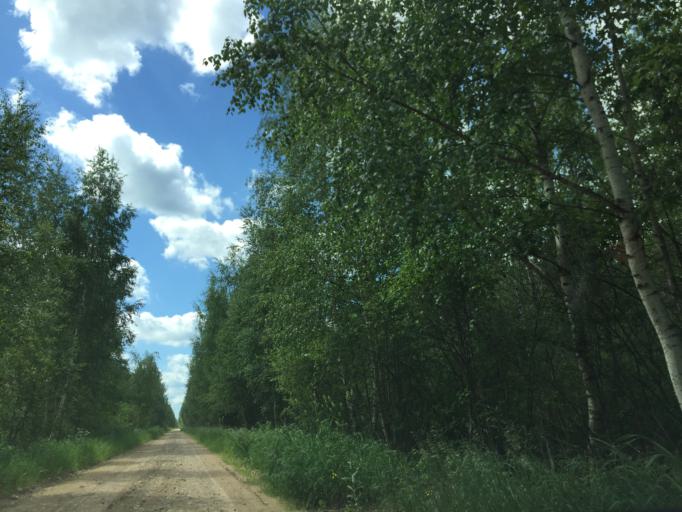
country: LV
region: Olaine
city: Olaine
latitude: 56.8502
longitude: 23.9427
